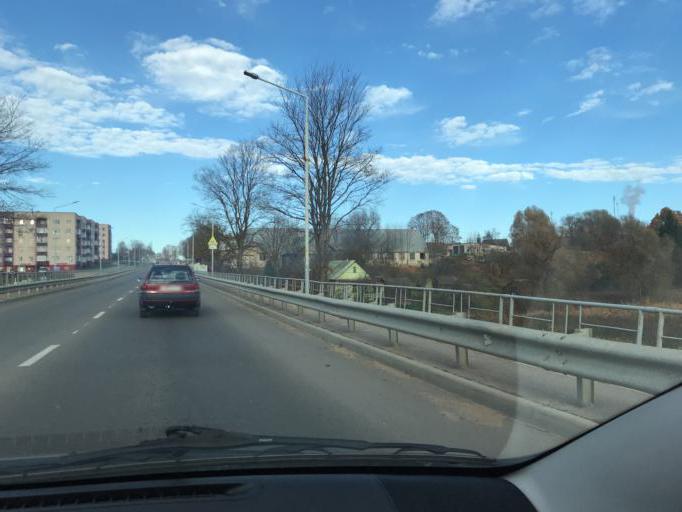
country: BY
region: Vitebsk
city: Haradok
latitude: 55.4677
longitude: 29.9756
